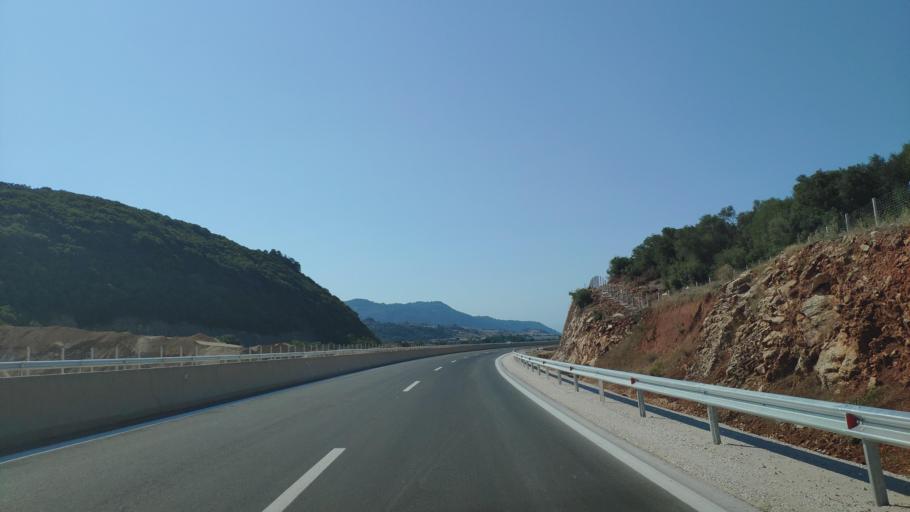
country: GR
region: West Greece
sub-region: Nomos Aitolias kai Akarnanias
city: Stanos
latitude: 38.7818
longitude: 21.1452
